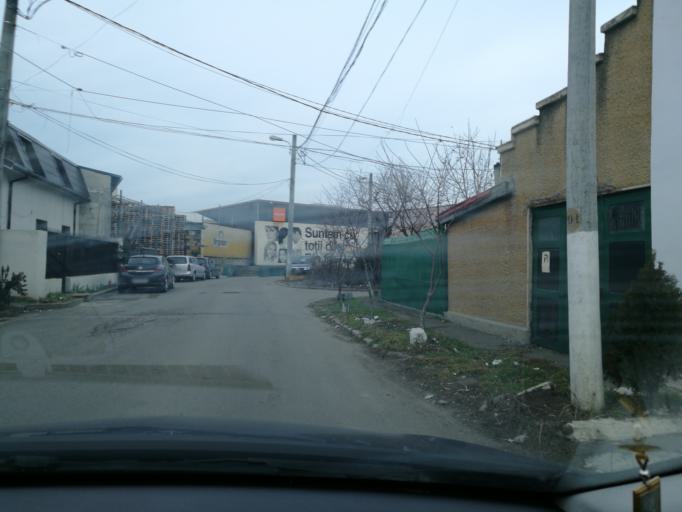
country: RO
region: Constanta
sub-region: Municipiul Constanta
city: Constanta
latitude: 44.1724
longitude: 28.6091
